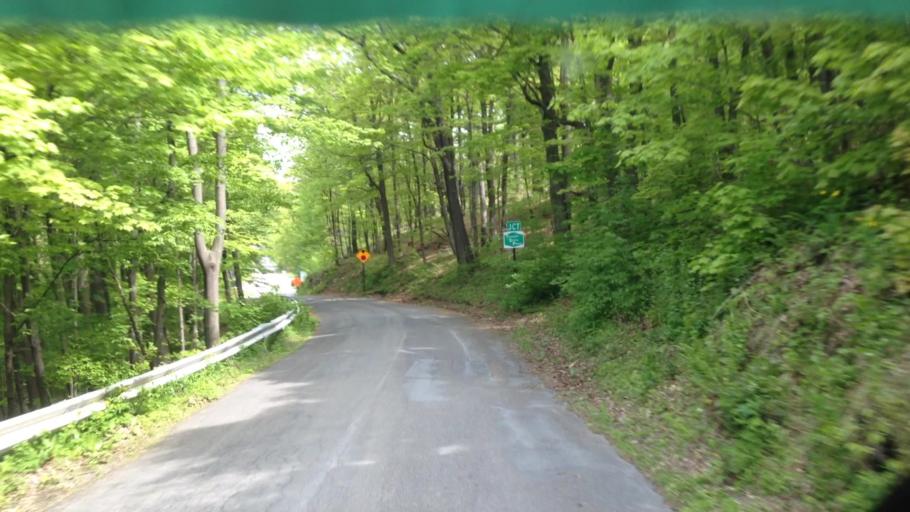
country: US
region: New York
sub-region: Dutchess County
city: Pine Plains
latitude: 41.9265
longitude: -73.7620
